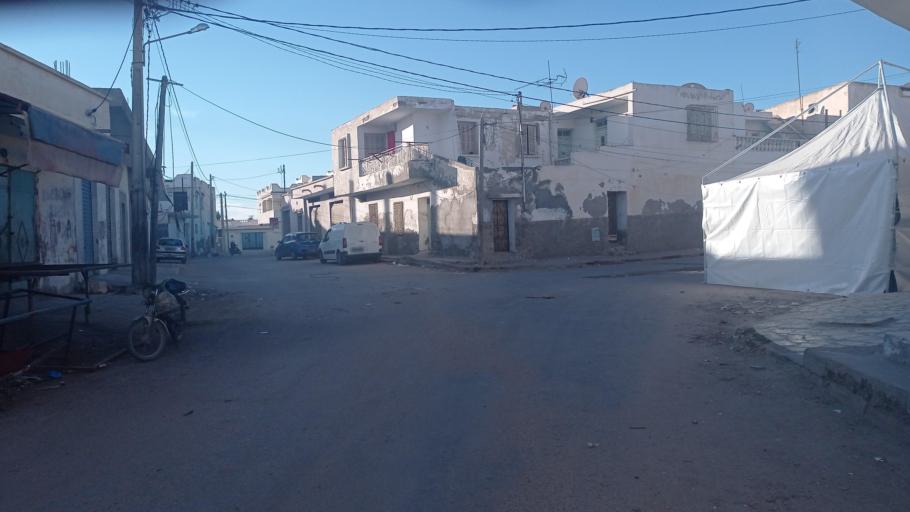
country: TN
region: Qabis
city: Gabes
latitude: 33.8430
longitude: 10.1197
